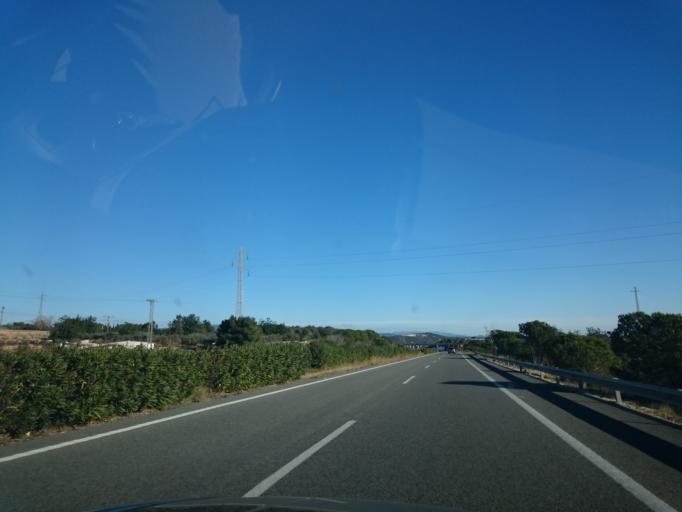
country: ES
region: Catalonia
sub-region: Provincia de Tarragona
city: Amposta
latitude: 40.7144
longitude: 0.5575
